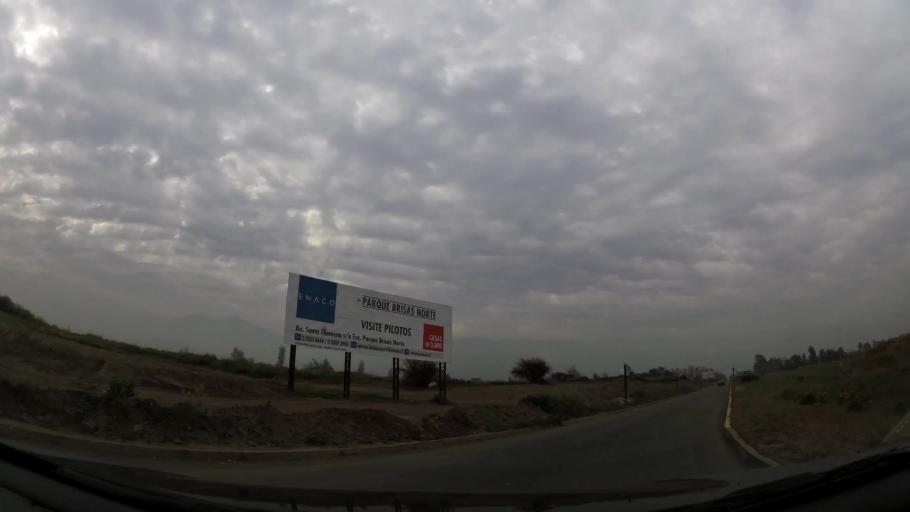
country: CL
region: Santiago Metropolitan
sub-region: Provincia de Chacabuco
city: Chicureo Abajo
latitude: -33.2150
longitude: -70.6733
